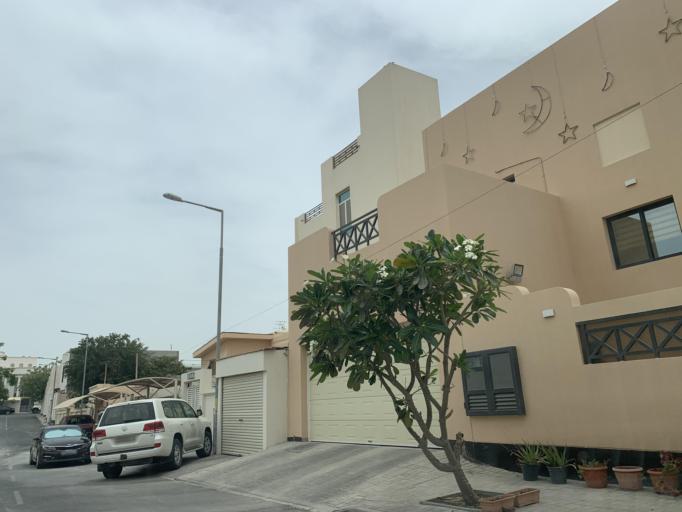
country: BH
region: Northern
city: Ar Rifa'
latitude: 26.1374
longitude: 50.5526
